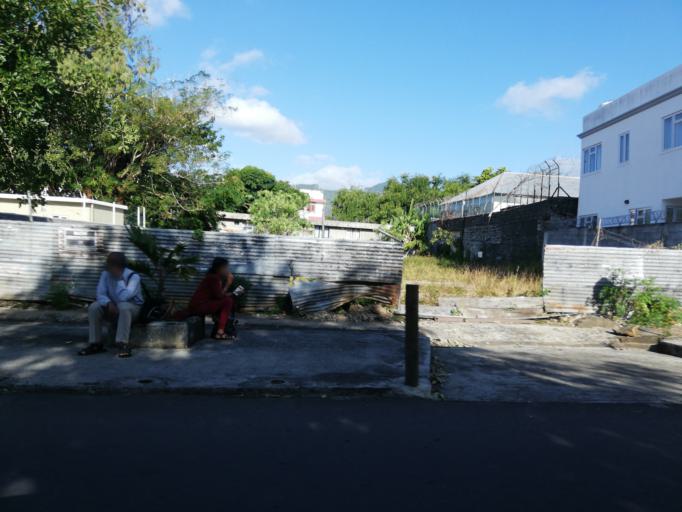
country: MU
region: Port Louis
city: Port Louis
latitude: -20.1621
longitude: 57.4900
